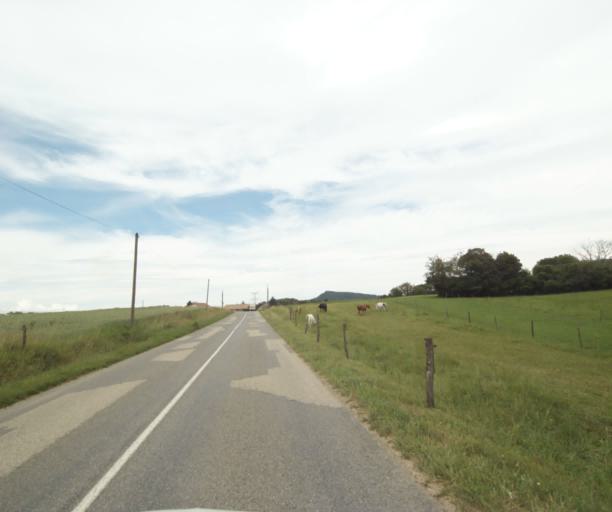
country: FR
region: Rhone-Alpes
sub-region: Departement de la Haute-Savoie
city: Perrignier
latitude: 46.2942
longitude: 6.4163
